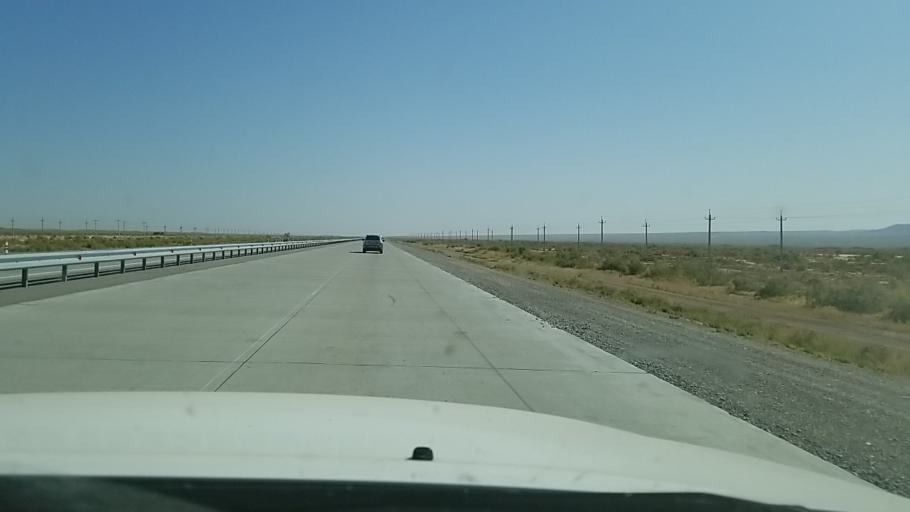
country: KZ
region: Almaty Oblysy
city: Kegen
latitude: 43.7426
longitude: 78.8338
